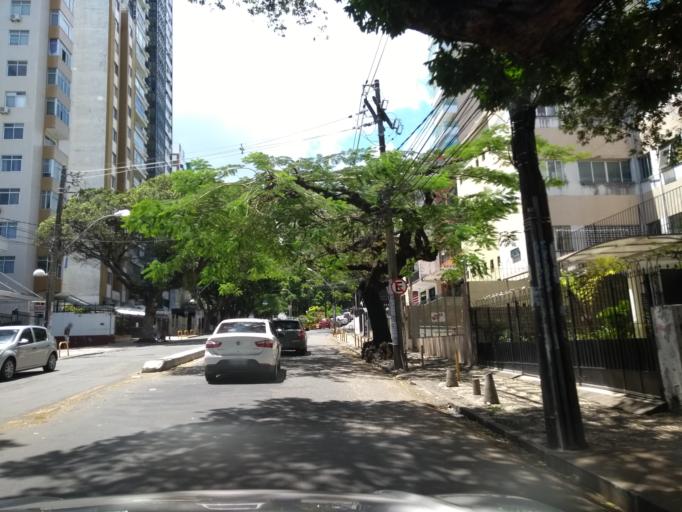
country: BR
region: Bahia
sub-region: Salvador
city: Salvador
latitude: -13.0019
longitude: -38.5241
